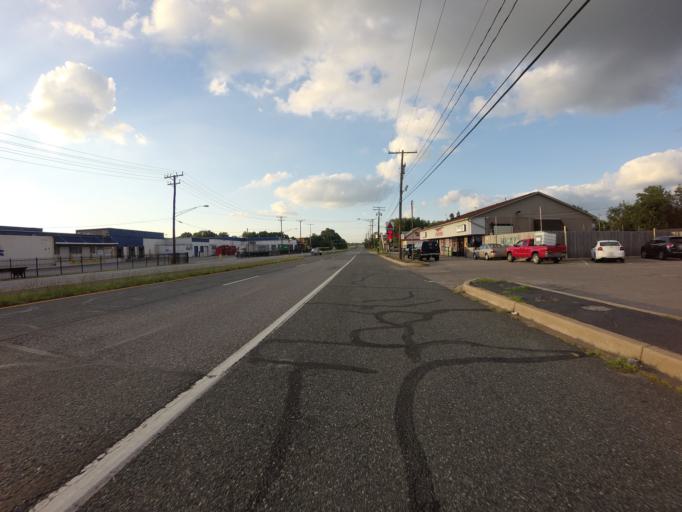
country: US
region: Maryland
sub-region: Baltimore County
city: Edgemere
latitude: 39.2348
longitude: -76.4567
